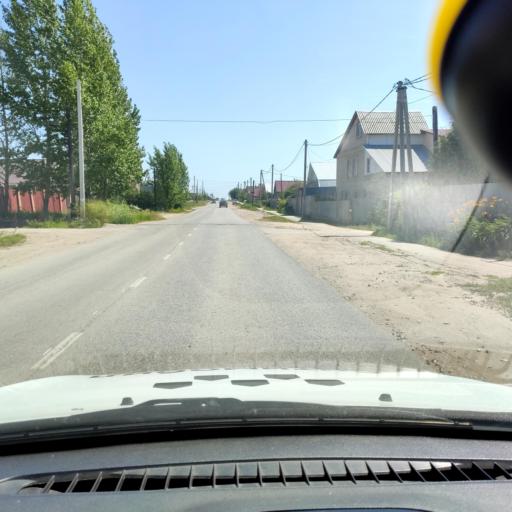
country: RU
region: Samara
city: Zhigulevsk
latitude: 53.3807
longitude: 49.4619
